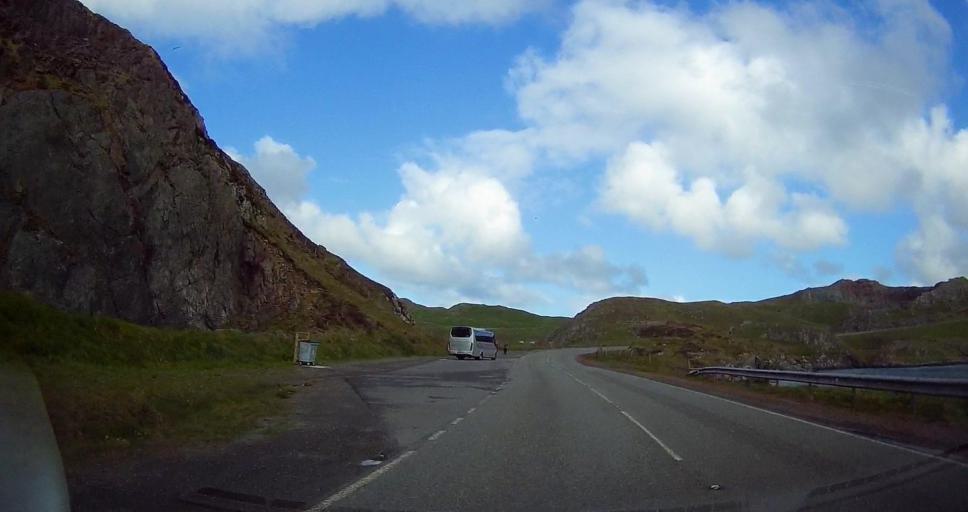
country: GB
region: Scotland
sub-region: Shetland Islands
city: Lerwick
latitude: 60.3969
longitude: -1.3825
